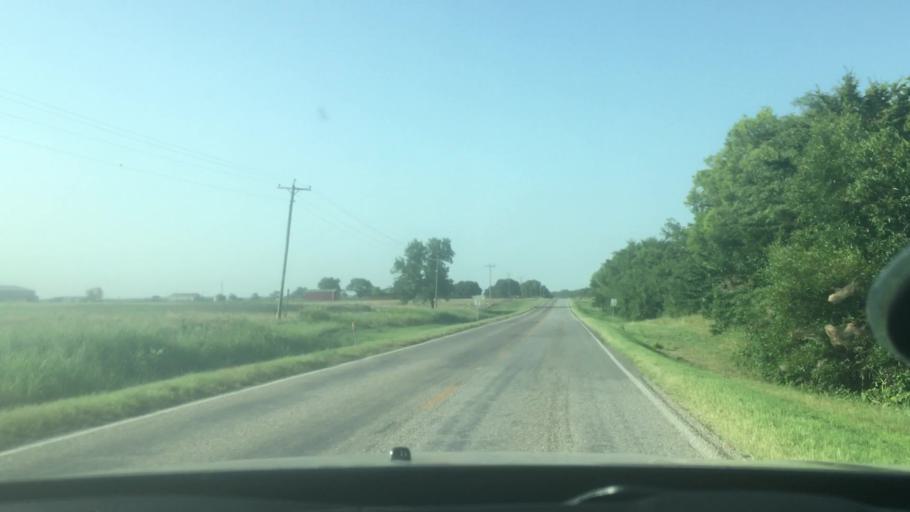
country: US
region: Oklahoma
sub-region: Coal County
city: Coalgate
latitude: 34.3632
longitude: -96.4245
